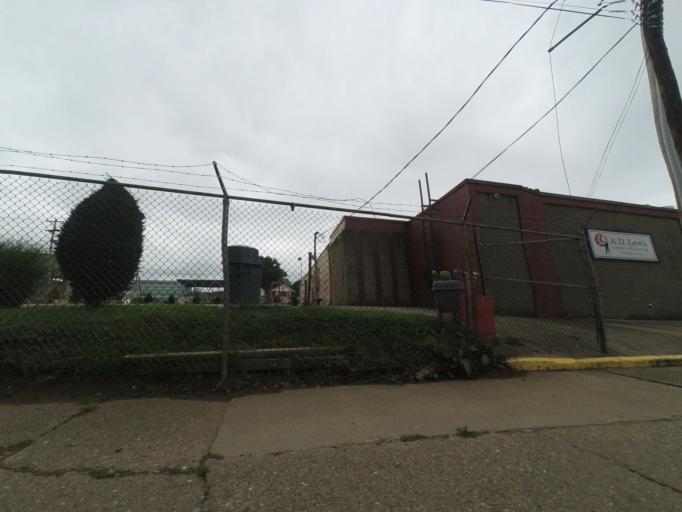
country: US
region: West Virginia
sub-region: Cabell County
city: Huntington
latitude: 38.4136
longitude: -82.4303
